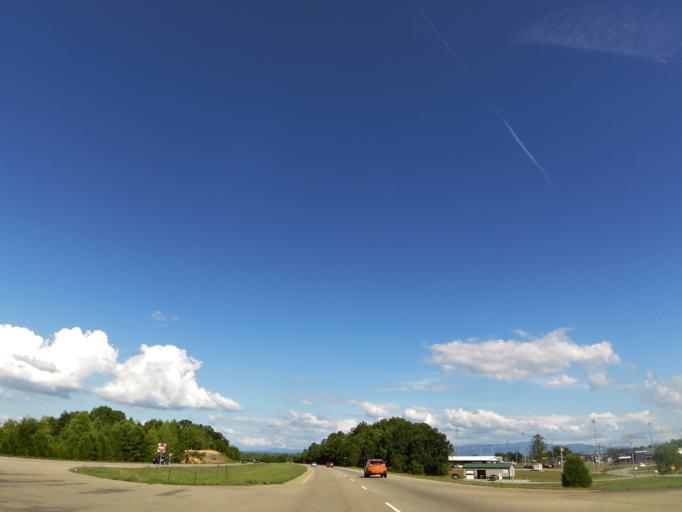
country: US
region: Tennessee
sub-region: Greene County
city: Mosheim
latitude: 36.1877
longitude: -82.9767
